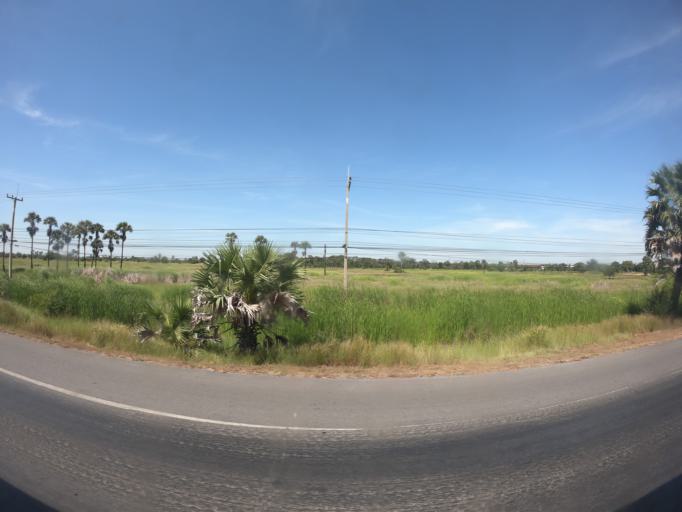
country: TH
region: Nakhon Ratchasima
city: Non Sung
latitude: 15.1624
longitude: 102.3314
